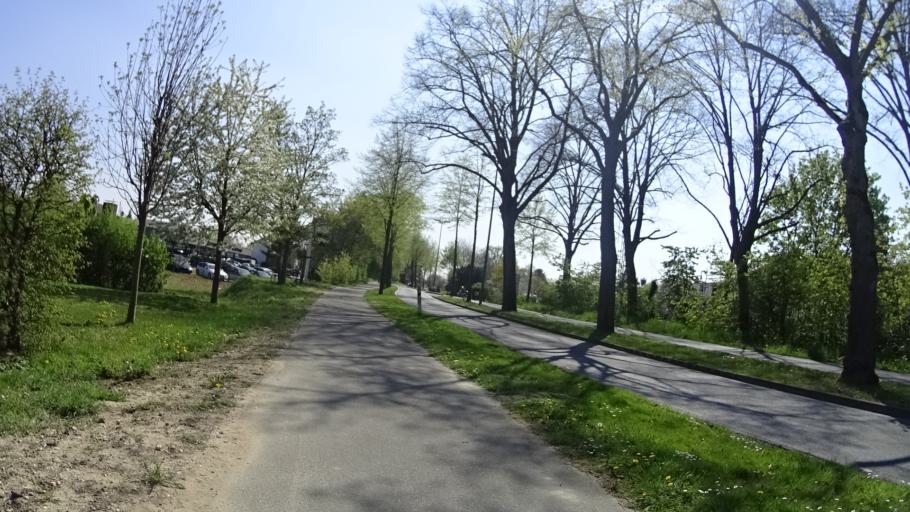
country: DE
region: North Rhine-Westphalia
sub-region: Regierungsbezirk Dusseldorf
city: Meerbusch
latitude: 51.3148
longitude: 6.6792
